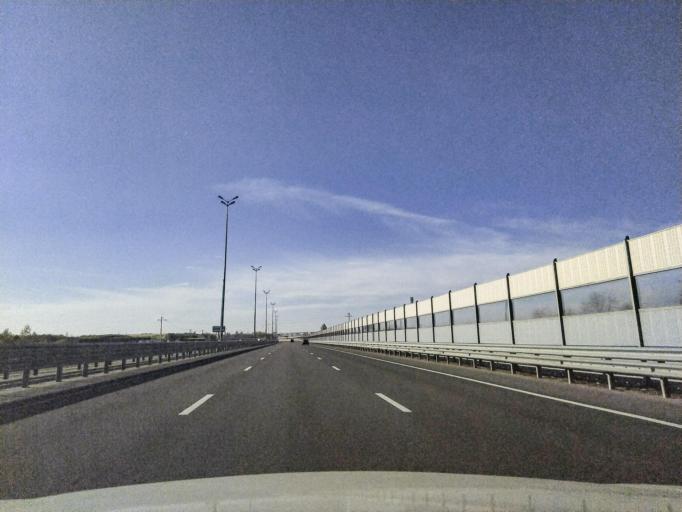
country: RU
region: Leningrad
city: Mariyenburg
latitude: 59.5260
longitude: 30.0930
